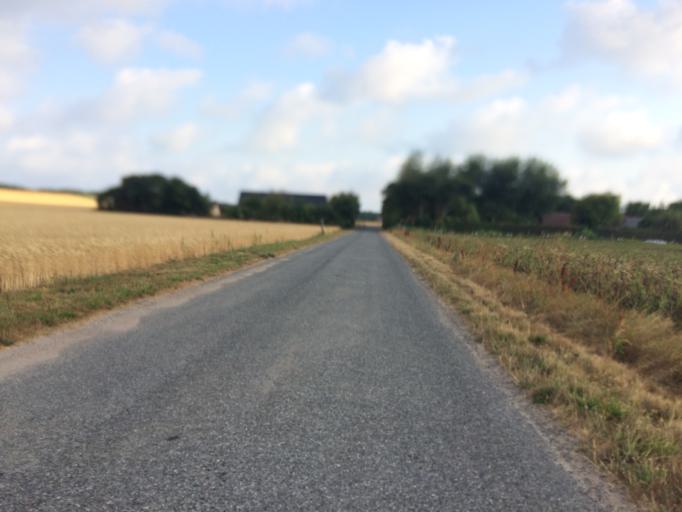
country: DK
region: Central Jutland
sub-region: Holstebro Kommune
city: Vinderup
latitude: 56.6077
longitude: 8.7187
